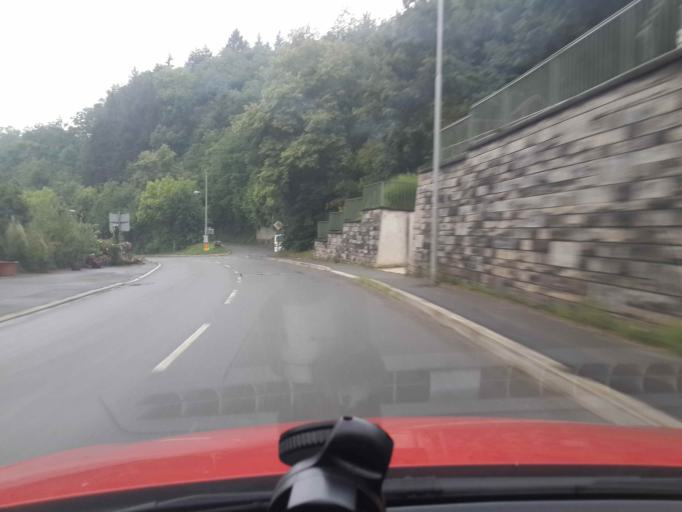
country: DE
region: Baden-Wuerttemberg
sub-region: Karlsruhe Region
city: Billigheim
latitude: 49.3260
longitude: 9.2394
